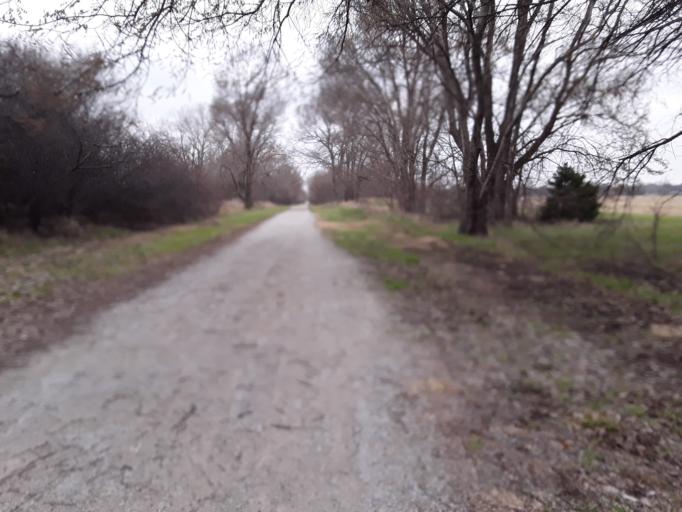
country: US
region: Nebraska
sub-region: Lancaster County
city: Lincoln
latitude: 40.8514
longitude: -96.6129
